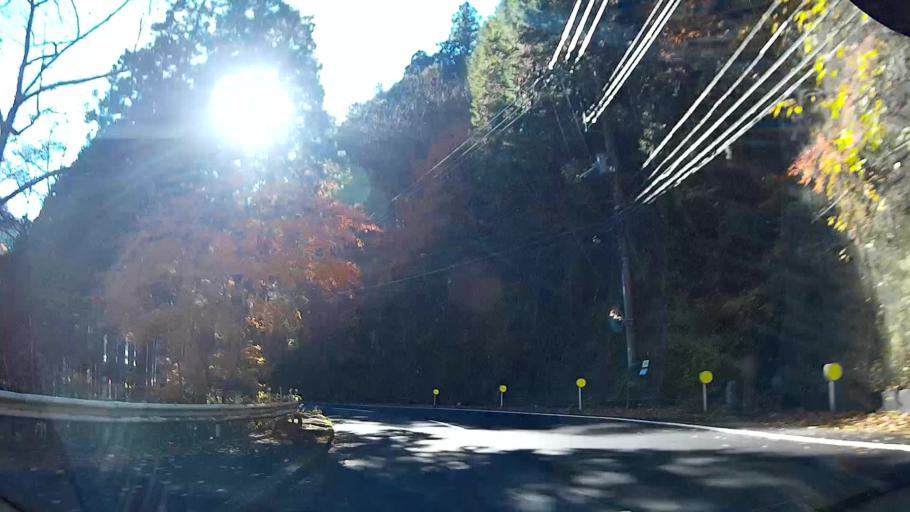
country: JP
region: Tokyo
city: Itsukaichi
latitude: 35.7079
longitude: 139.1526
